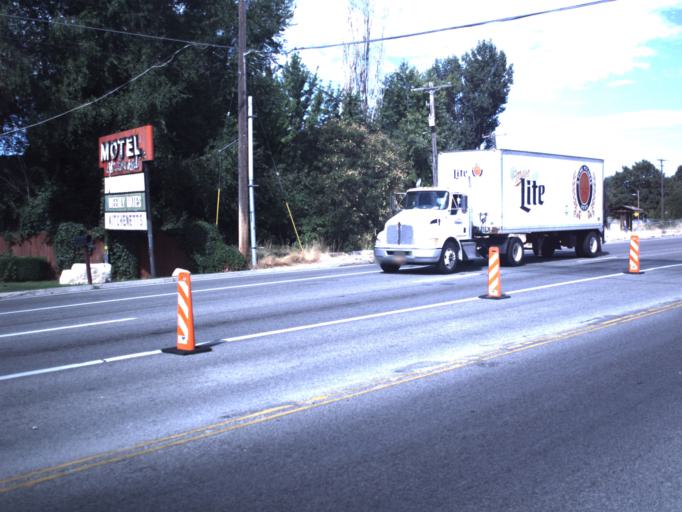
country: US
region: Utah
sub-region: Weber County
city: Harrisville
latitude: 41.2716
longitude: -111.9779
